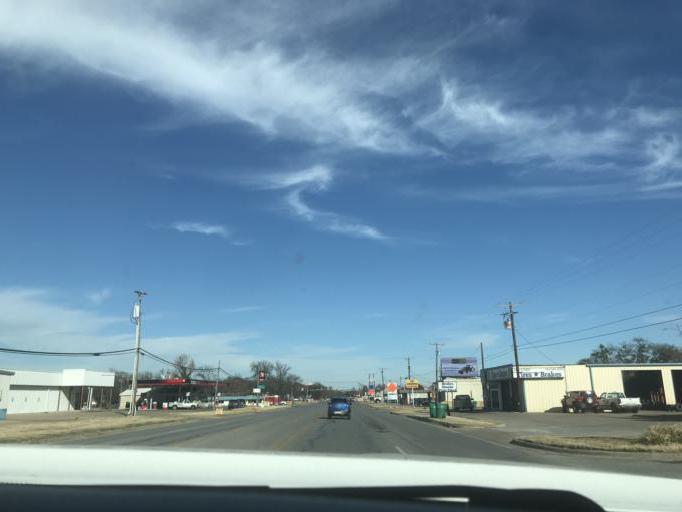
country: US
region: Texas
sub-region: Erath County
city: Stephenville
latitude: 32.2306
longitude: -98.2130
